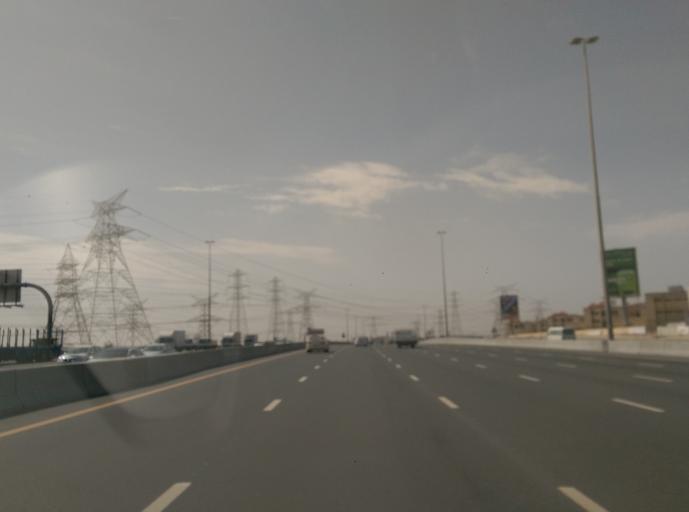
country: AE
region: Dubai
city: Dubai
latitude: 25.1408
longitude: 55.2607
